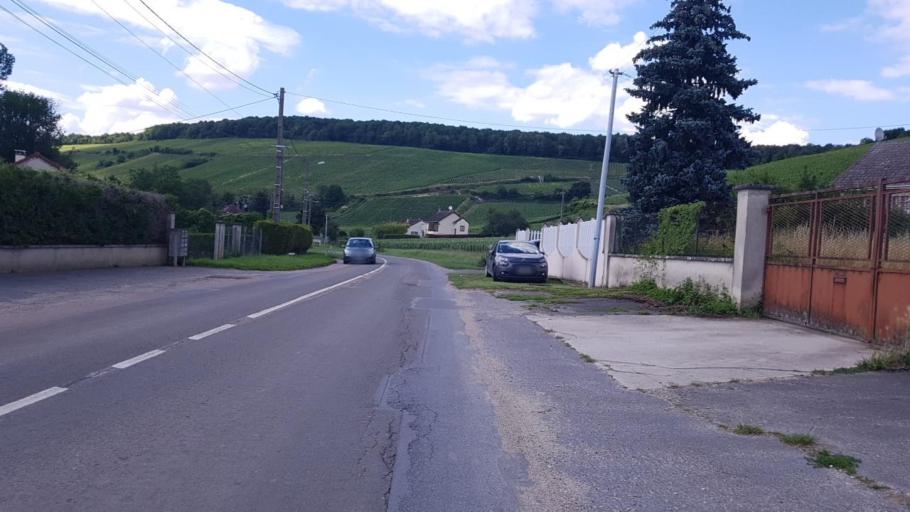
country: FR
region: Picardie
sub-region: Departement de l'Aisne
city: Crezancy
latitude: 49.0812
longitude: 3.5593
